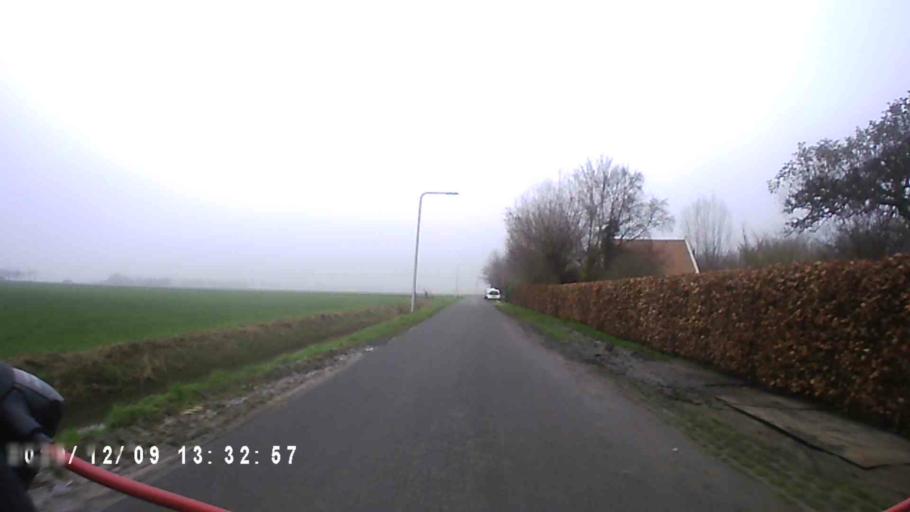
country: NL
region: Groningen
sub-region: Gemeente Bedum
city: Bedum
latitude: 53.2787
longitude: 6.6010
